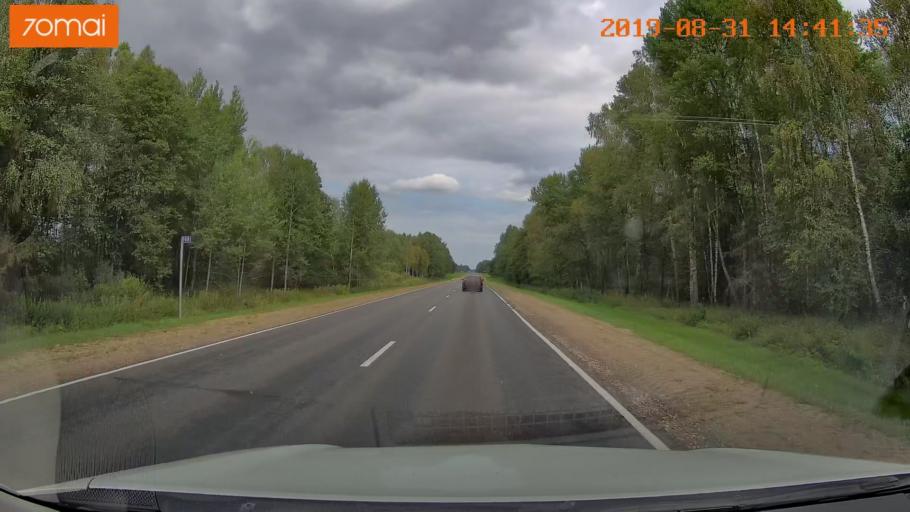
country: RU
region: Smolensk
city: Yekimovichi
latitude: 54.2033
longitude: 33.5922
